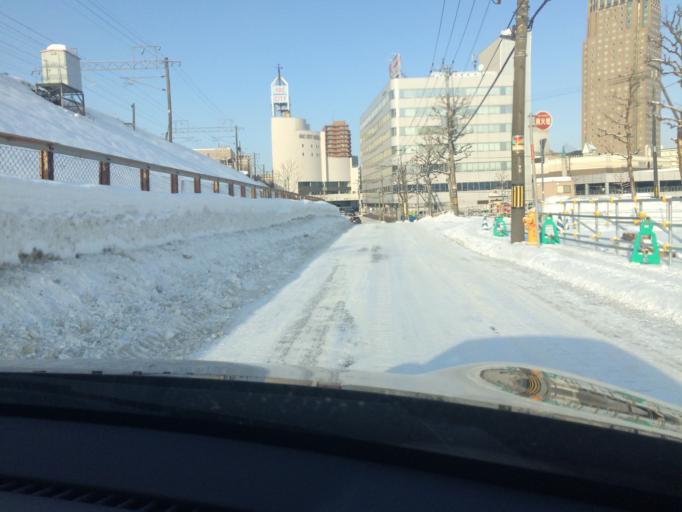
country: JP
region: Hokkaido
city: Ebetsu
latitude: 43.0379
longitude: 141.4761
